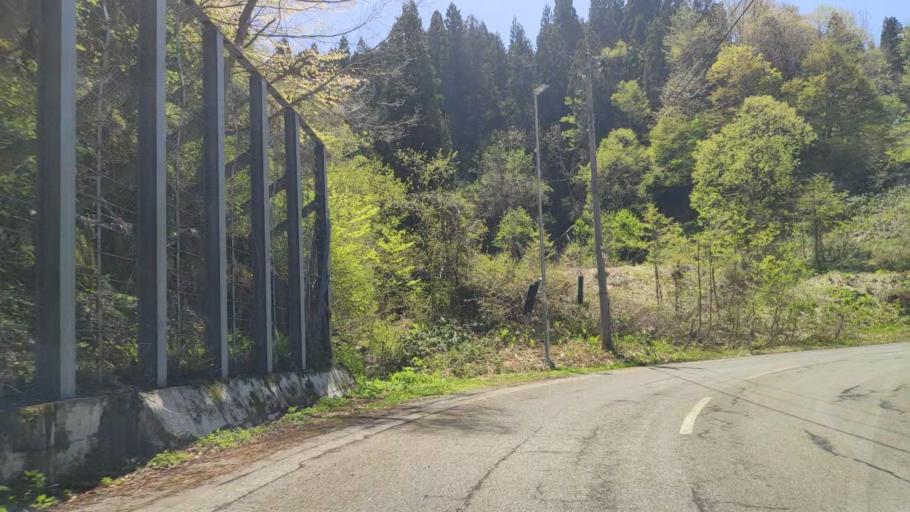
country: JP
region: Yamagata
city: Shinjo
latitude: 38.9727
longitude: 140.3553
